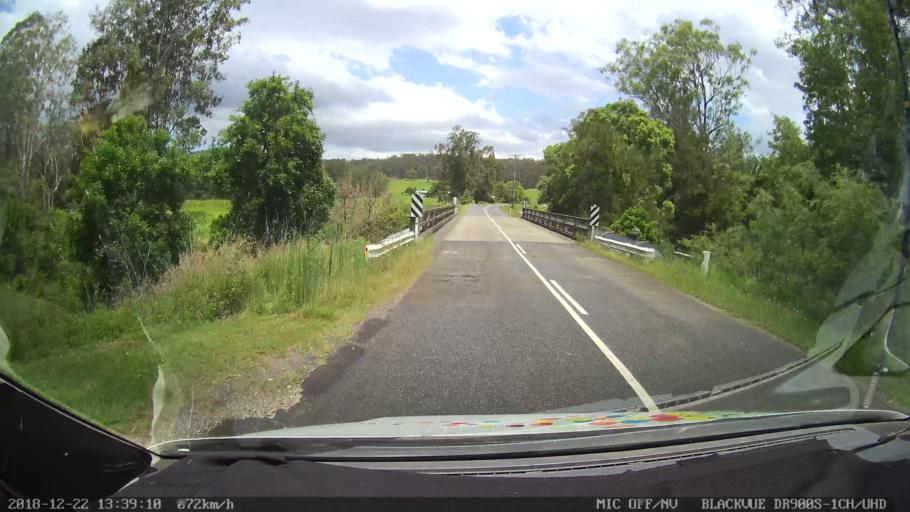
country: AU
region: New South Wales
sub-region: Clarence Valley
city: Coutts Crossing
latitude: -29.9080
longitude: 152.7864
